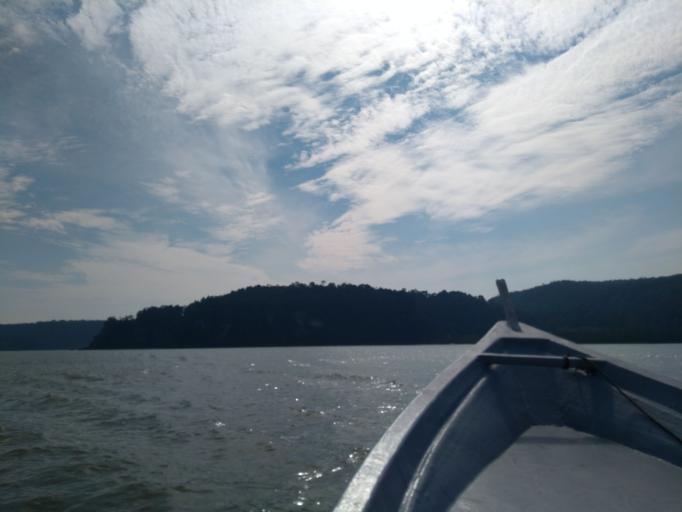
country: MY
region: Sarawak
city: Kuching
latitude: 1.7096
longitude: 110.4348
